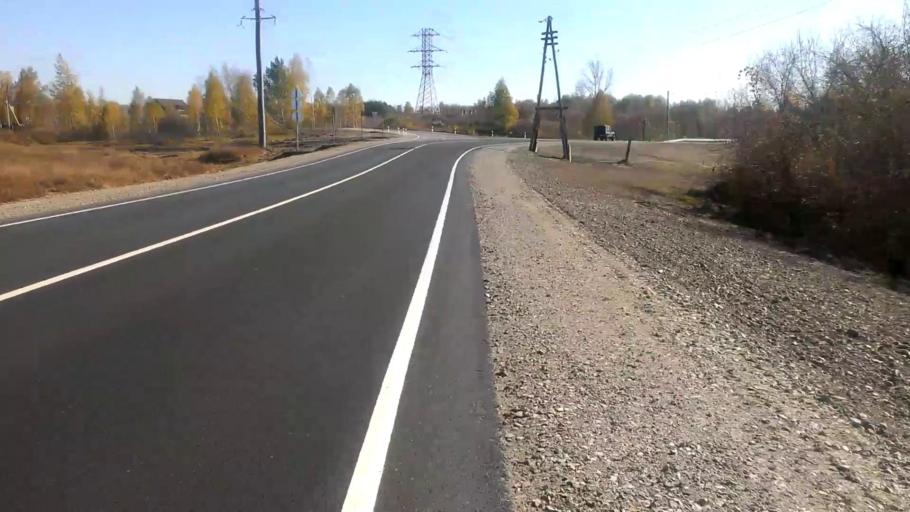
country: RU
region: Altai Krai
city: Sannikovo
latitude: 53.3285
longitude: 83.9403
